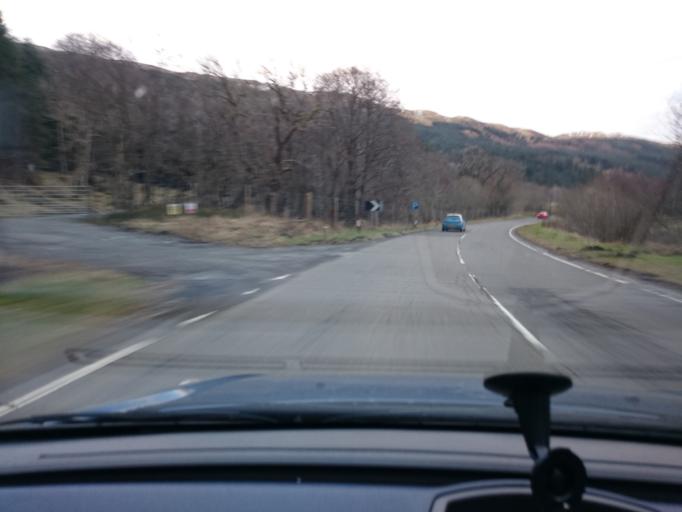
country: GB
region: Scotland
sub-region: Stirling
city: Callander
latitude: 56.2958
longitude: -4.2929
